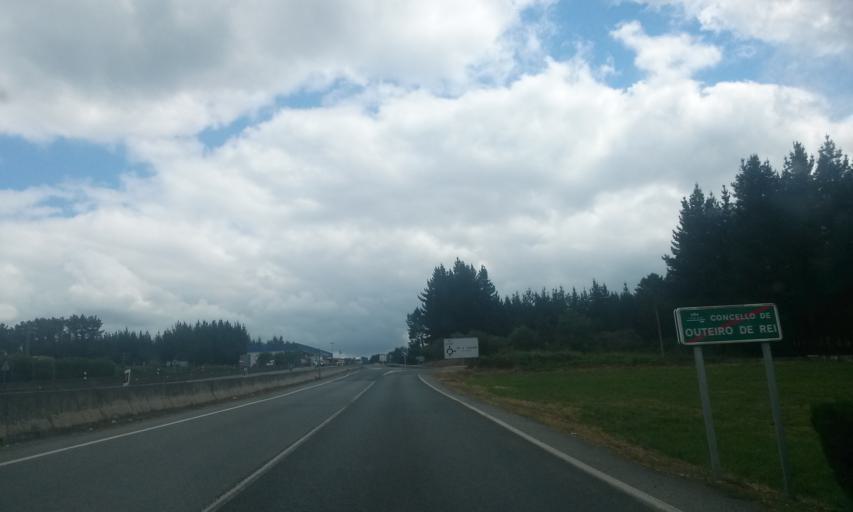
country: ES
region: Galicia
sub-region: Provincia de Lugo
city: Outeiro de Rei
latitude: 43.0602
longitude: -7.5999
